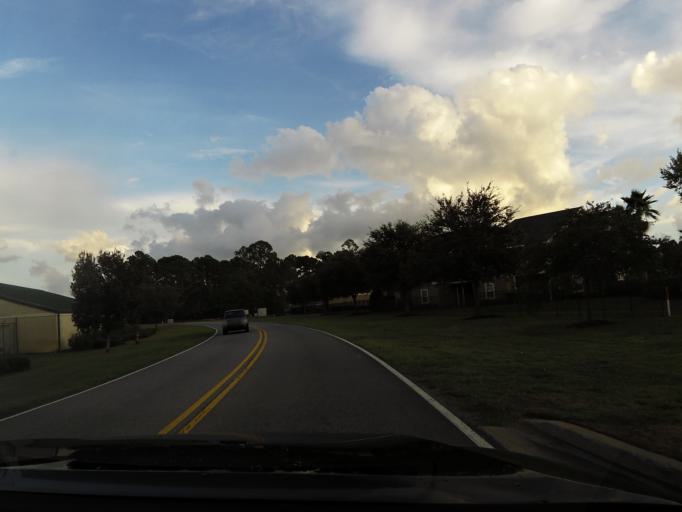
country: US
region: Georgia
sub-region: Glynn County
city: Country Club Estates
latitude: 31.2121
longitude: -81.4838
